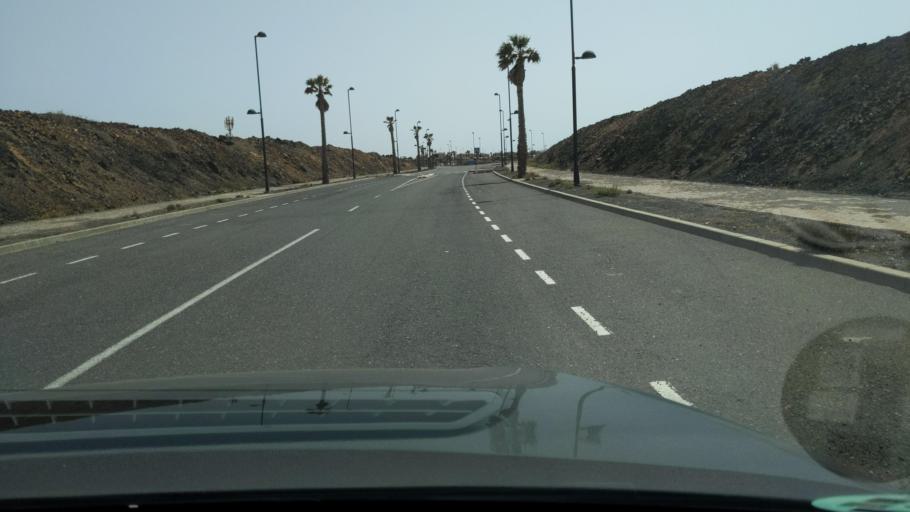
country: ES
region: Canary Islands
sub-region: Provincia de Las Palmas
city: Corralejo
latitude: 28.7359
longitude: -13.9449
